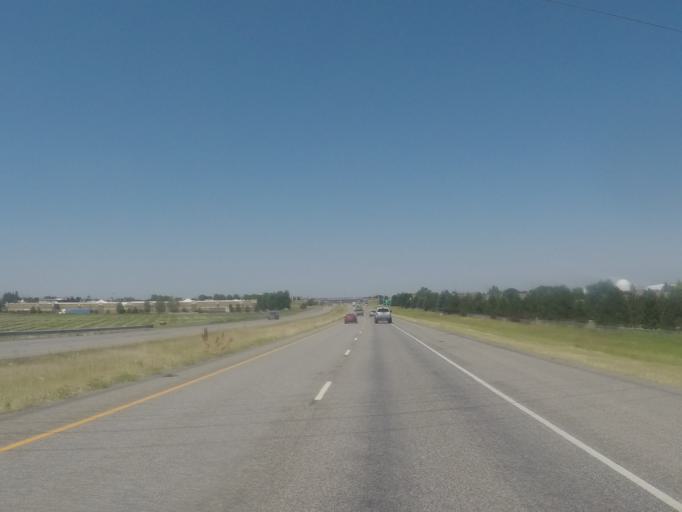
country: US
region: Montana
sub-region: Gallatin County
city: Bozeman
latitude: 45.6948
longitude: -111.0358
